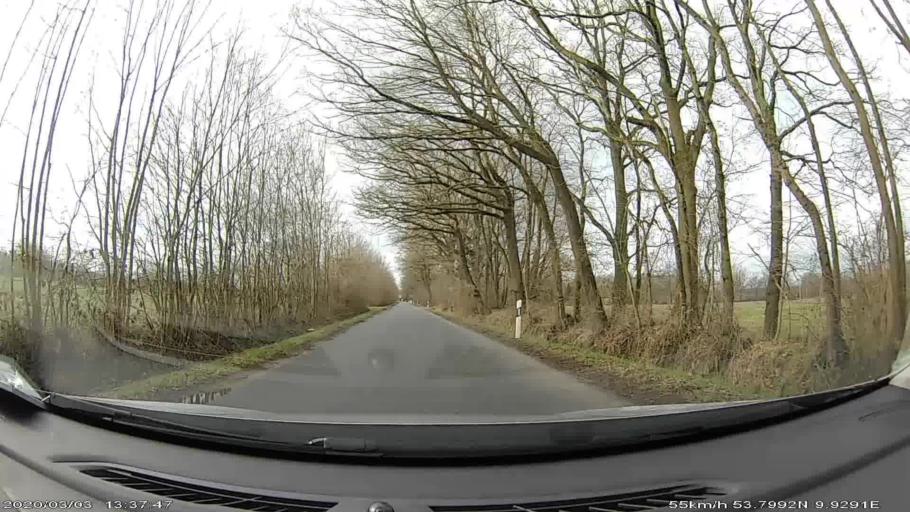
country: DE
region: Schleswig-Holstein
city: Alveslohe
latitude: 53.7996
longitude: 9.9273
